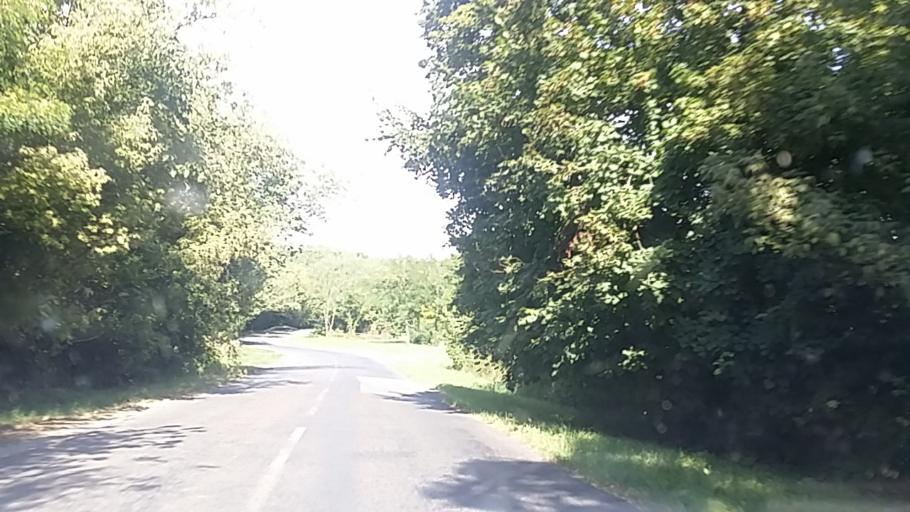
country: HU
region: Tolna
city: Hogyesz
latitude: 46.5255
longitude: 18.4266
